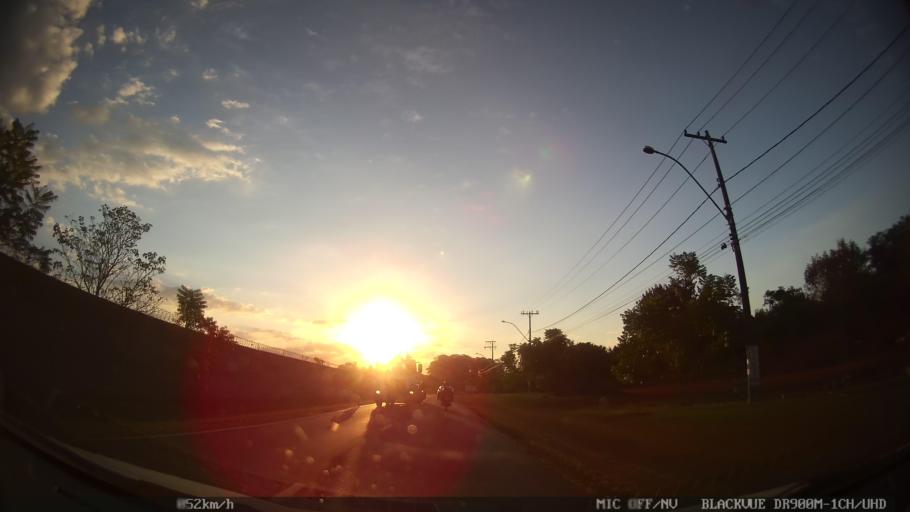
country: BR
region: Sao Paulo
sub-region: Ribeirao Preto
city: Ribeirao Preto
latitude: -21.1534
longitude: -47.7788
